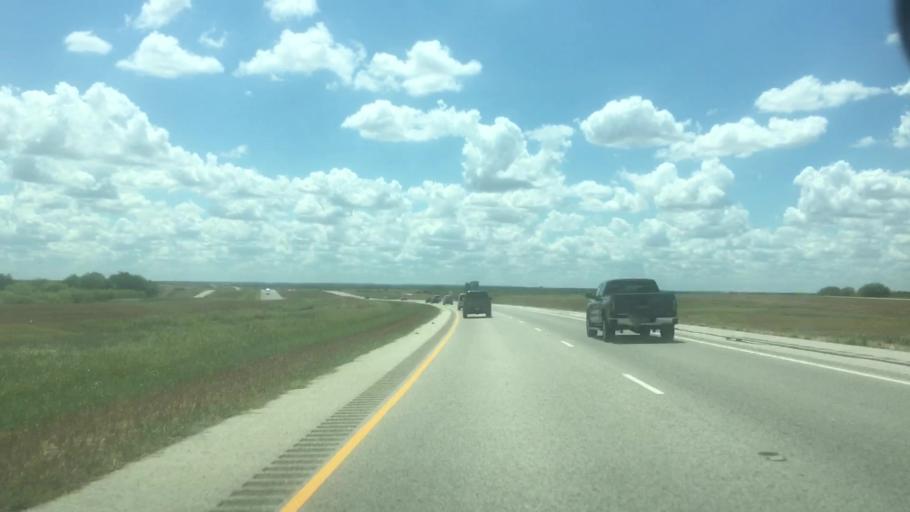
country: US
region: Texas
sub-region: Caldwell County
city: Martindale
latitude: 29.8045
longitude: -97.7756
